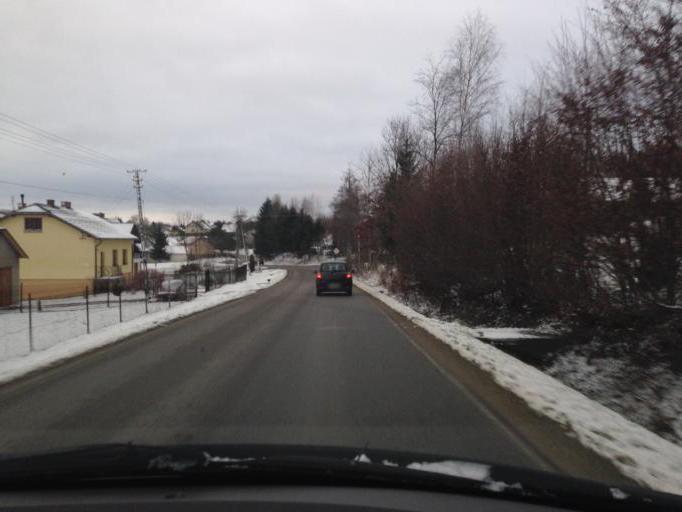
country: PL
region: Lesser Poland Voivodeship
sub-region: Powiat gorlicki
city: Moszczenica
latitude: 49.7417
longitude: 21.0838
